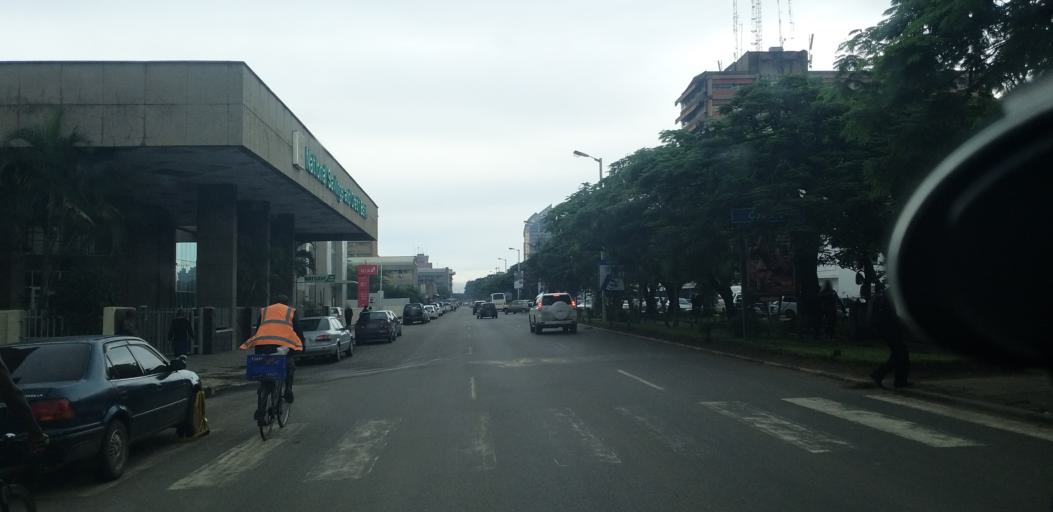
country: ZM
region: Lusaka
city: Lusaka
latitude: -15.4113
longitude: 28.2809
